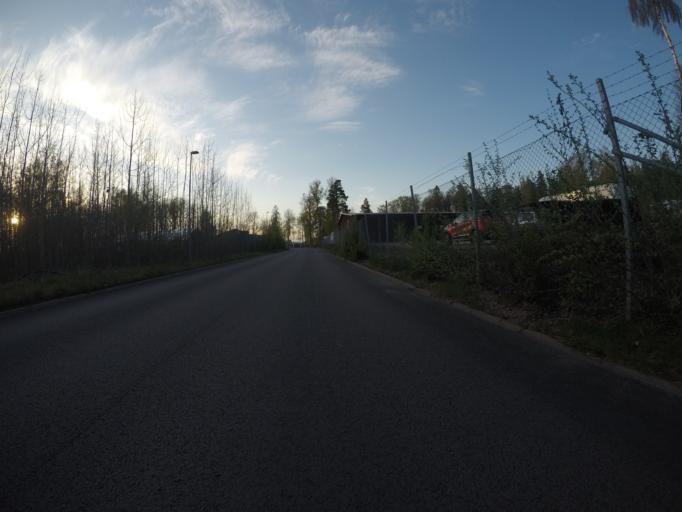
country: SE
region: Vaestmanland
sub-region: Vasteras
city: Vasteras
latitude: 59.5914
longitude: 16.6192
